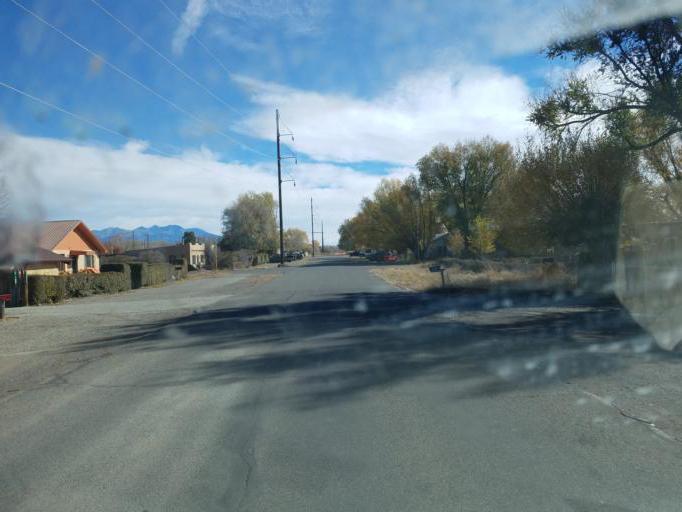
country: US
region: Colorado
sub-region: Alamosa County
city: Alamosa East
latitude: 37.4709
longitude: -105.8553
